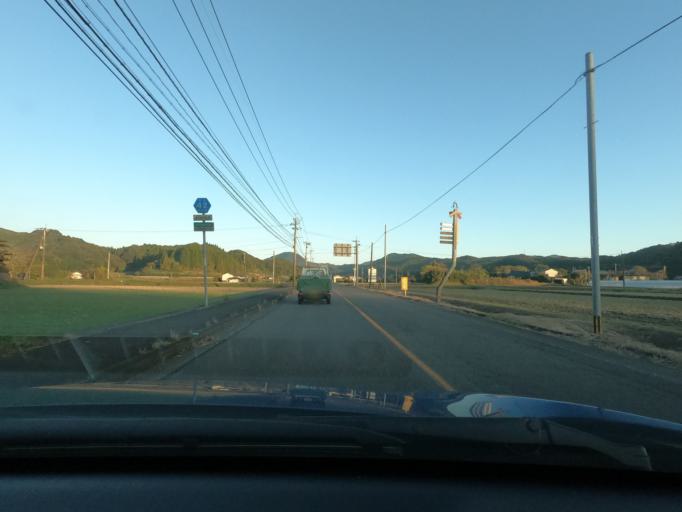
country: JP
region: Kagoshima
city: Satsumasendai
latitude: 31.7951
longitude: 130.4446
